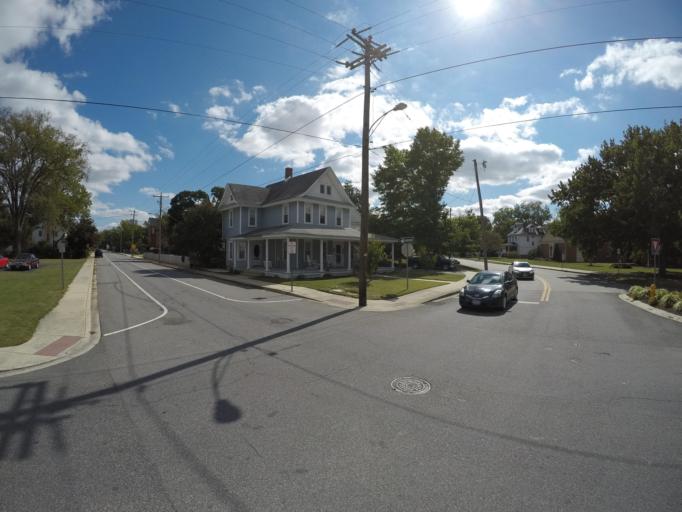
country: US
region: Maryland
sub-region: Caroline County
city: Denton
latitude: 38.8852
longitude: -75.8302
